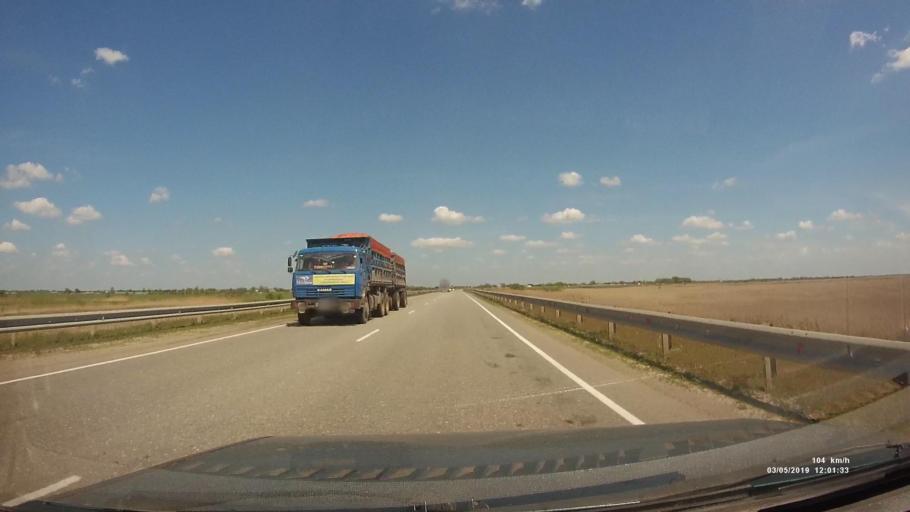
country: RU
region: Rostov
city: Bagayevskaya
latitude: 47.2643
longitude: 40.3520
